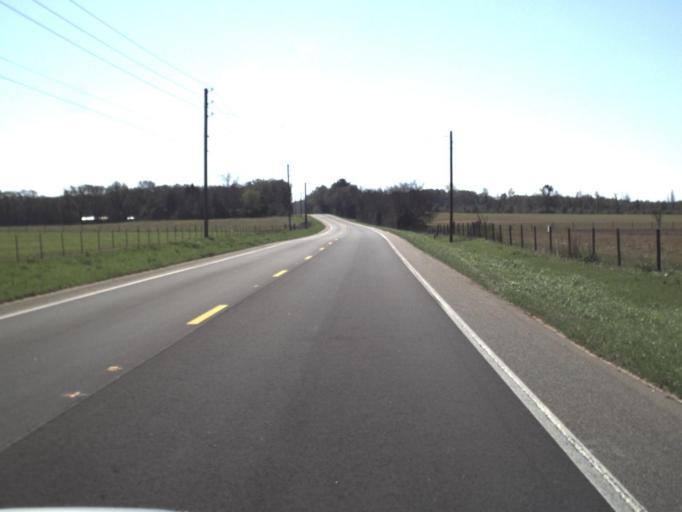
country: US
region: Florida
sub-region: Jackson County
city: Marianna
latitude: 30.6462
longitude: -85.1595
